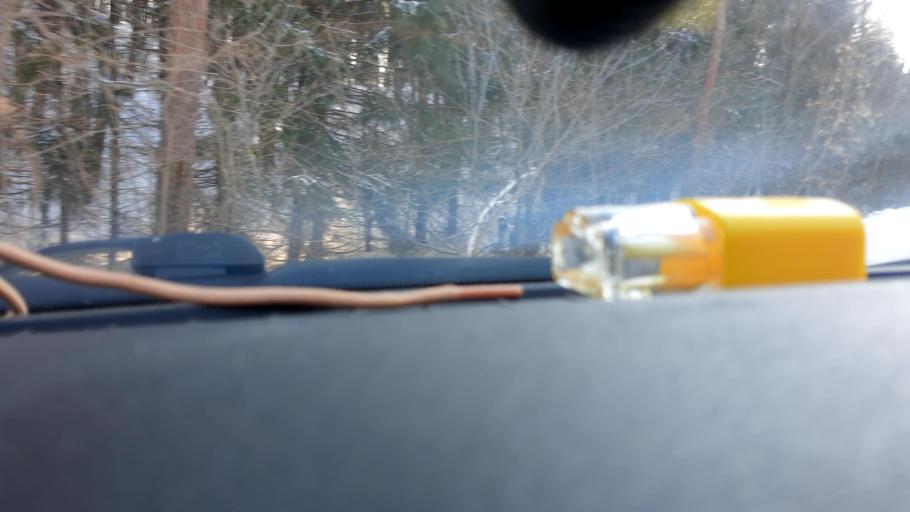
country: RU
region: Bashkortostan
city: Kabakovo
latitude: 54.6253
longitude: 56.0493
